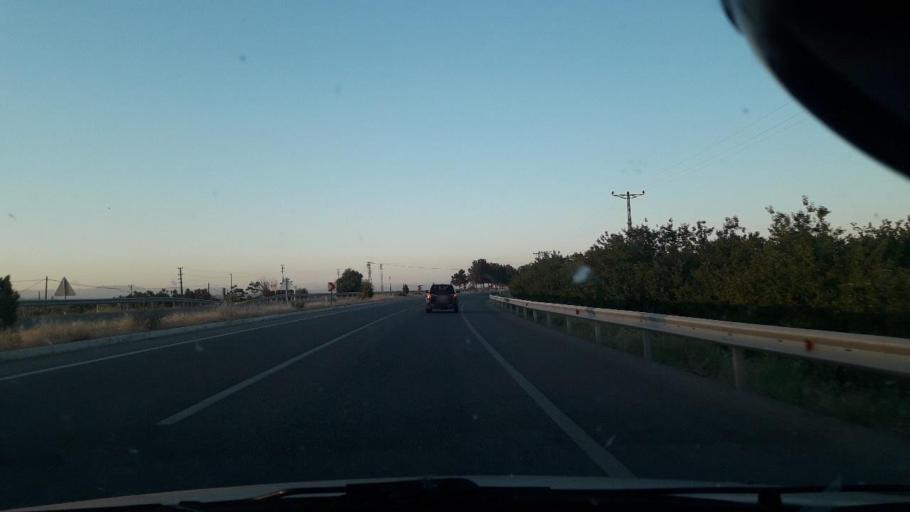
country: TR
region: Malatya
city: Yazihan
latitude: 38.4942
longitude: 38.2181
